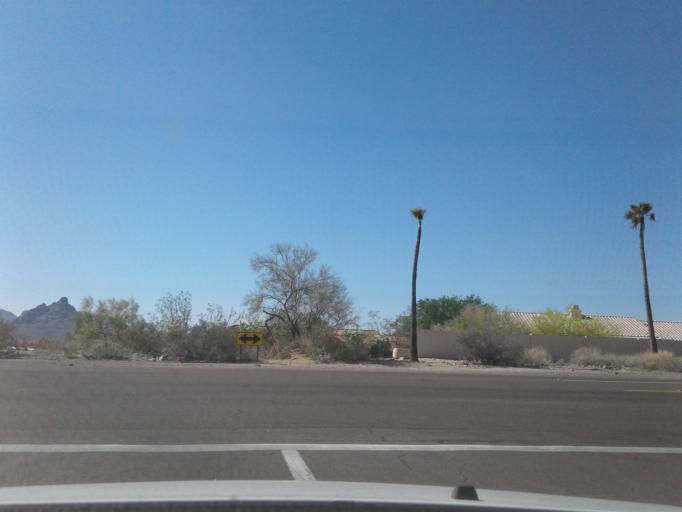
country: US
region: Arizona
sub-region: Maricopa County
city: Fountain Hills
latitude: 33.5870
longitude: -111.7371
